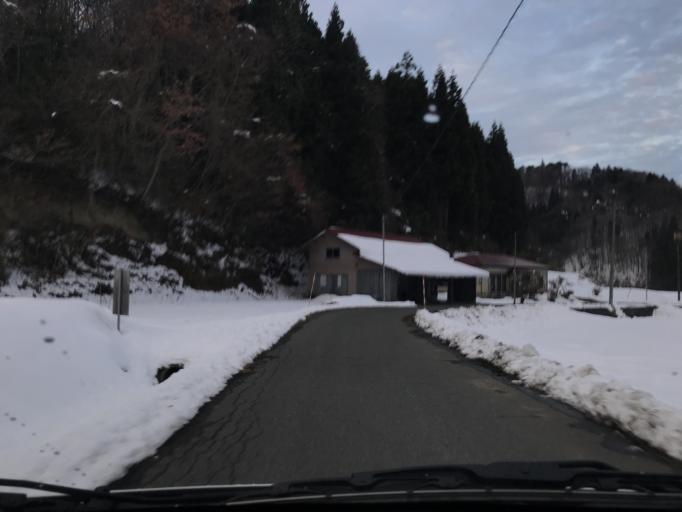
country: JP
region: Iwate
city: Mizusawa
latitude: 39.0455
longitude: 141.0124
